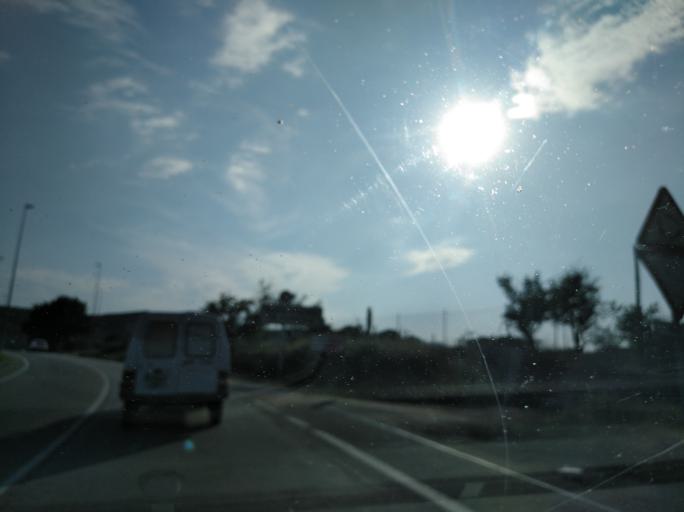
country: ES
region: Catalonia
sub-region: Provincia de Girona
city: Santa Coloma de Farners
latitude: 41.8564
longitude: 2.6808
